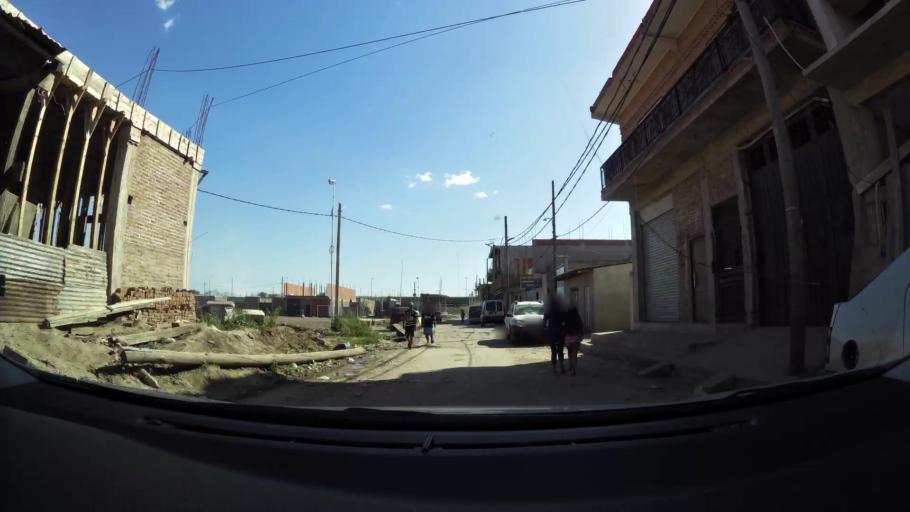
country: AR
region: Buenos Aires F.D.
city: Villa Lugano
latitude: -34.7103
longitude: -58.4833
